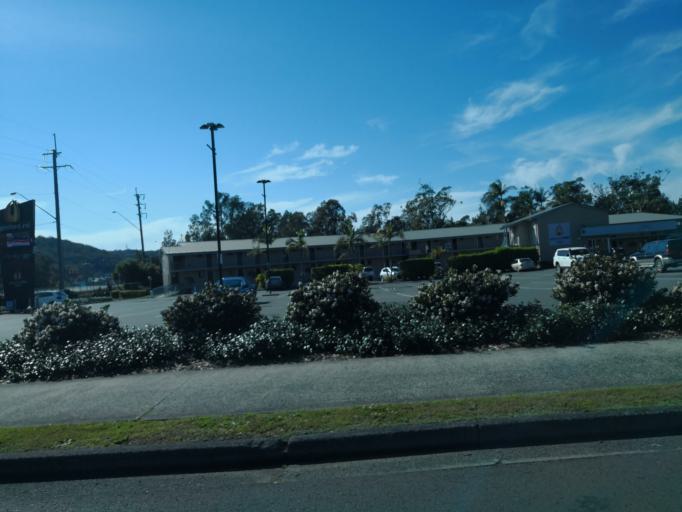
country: AU
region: New South Wales
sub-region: Gosford Shire
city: Point Clare
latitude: -33.4281
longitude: 151.3216
